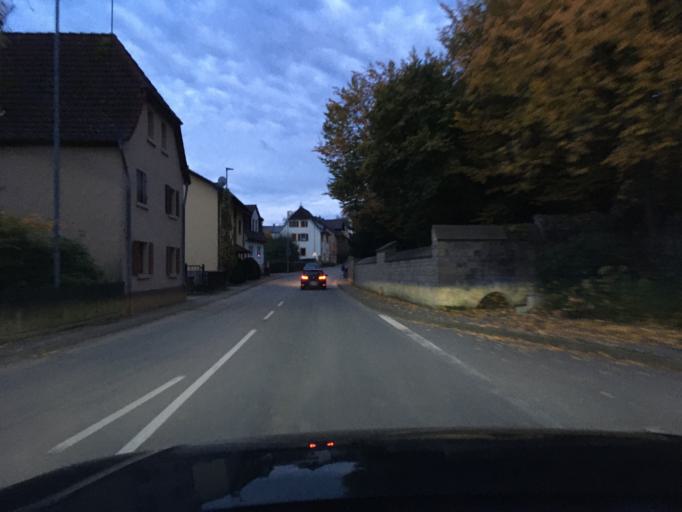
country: DE
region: Baden-Wuerttemberg
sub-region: Regierungsbezirk Stuttgart
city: Siegelsbach
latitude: 49.2418
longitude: 9.0588
